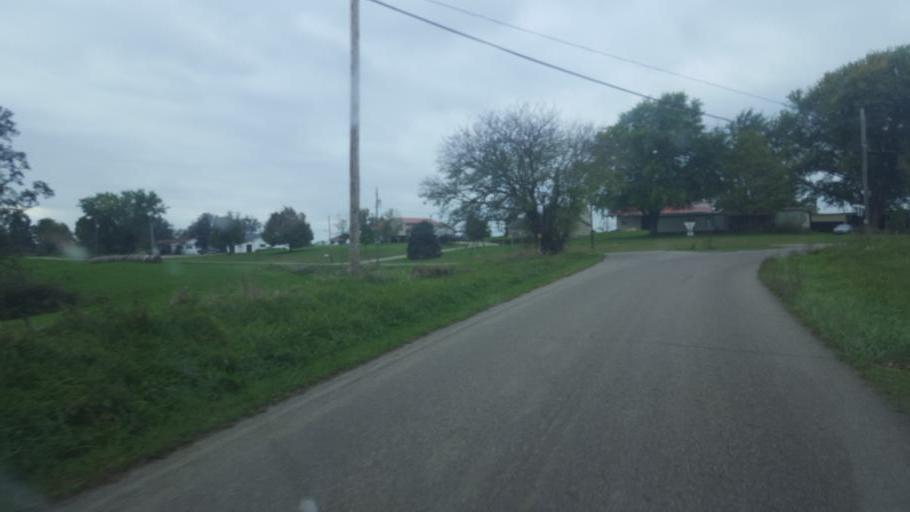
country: US
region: Ohio
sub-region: Harrison County
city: Cadiz
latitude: 40.3663
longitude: -81.0700
